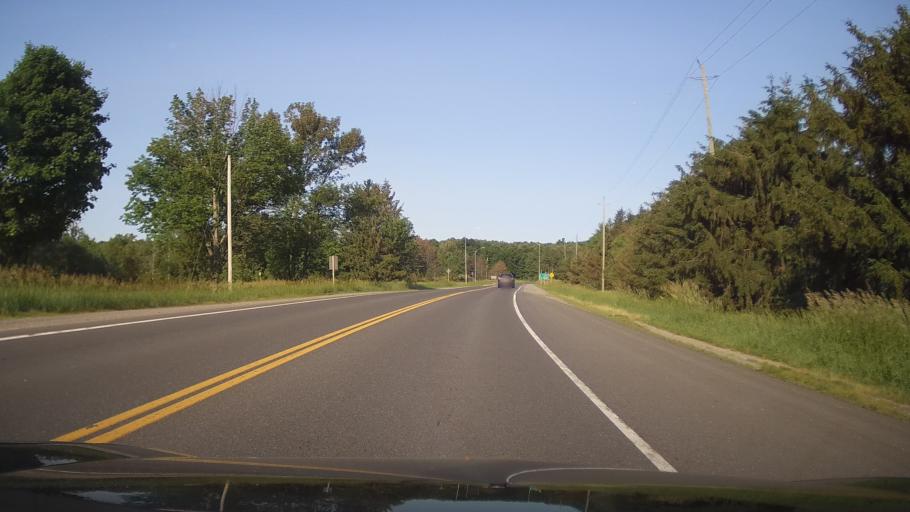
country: CA
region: Ontario
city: Quinte West
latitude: 44.5044
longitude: -77.4972
